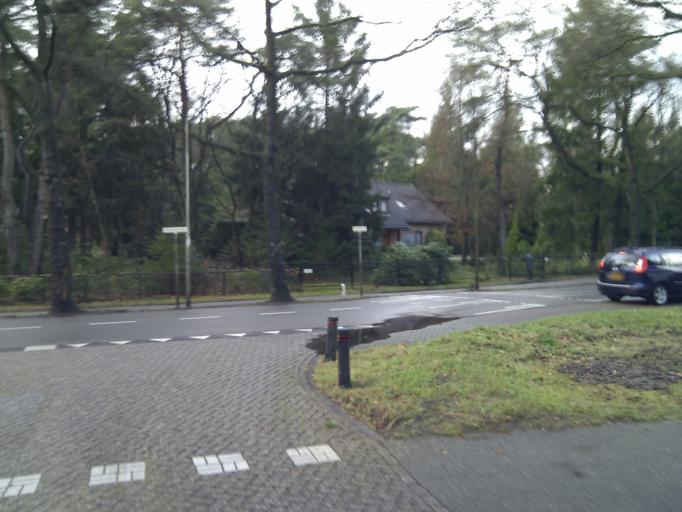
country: NL
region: Utrecht
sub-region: Gemeente Zeist
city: Zeist
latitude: 52.1154
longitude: 5.2396
